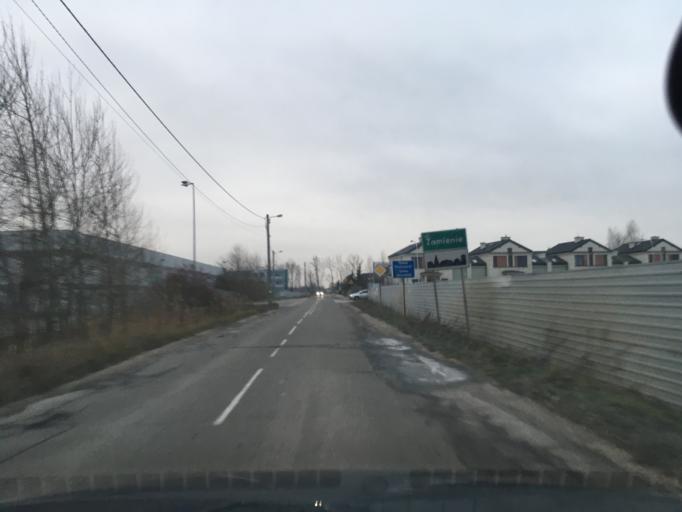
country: PL
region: Masovian Voivodeship
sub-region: Powiat piaseczynski
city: Mysiadlo
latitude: 52.1166
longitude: 20.9792
